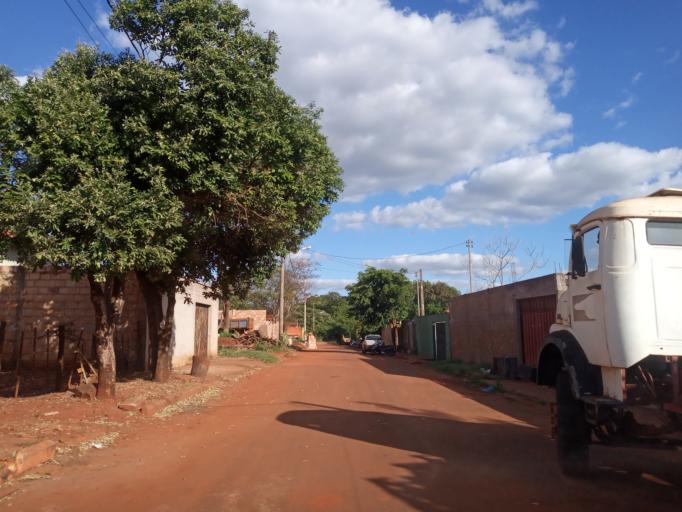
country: BR
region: Minas Gerais
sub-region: Ituiutaba
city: Ituiutaba
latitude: -18.9776
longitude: -49.4455
